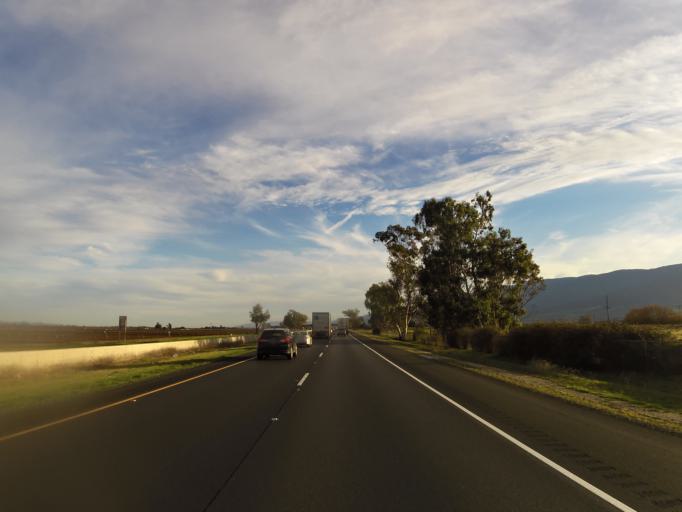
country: US
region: California
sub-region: Monterey County
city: Gonzales
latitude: 36.5004
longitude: -121.4311
